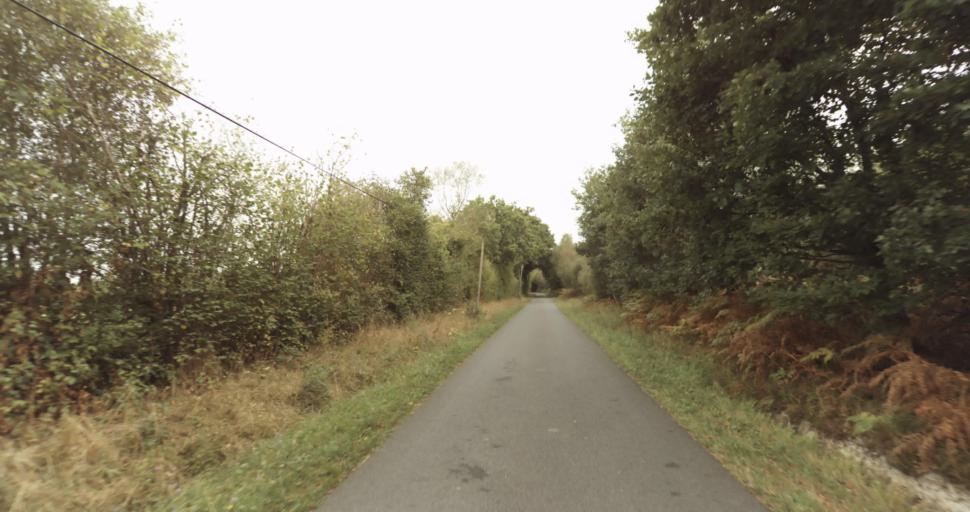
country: FR
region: Lower Normandy
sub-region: Departement de l'Orne
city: Gace
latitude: 48.8361
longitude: 0.3334
